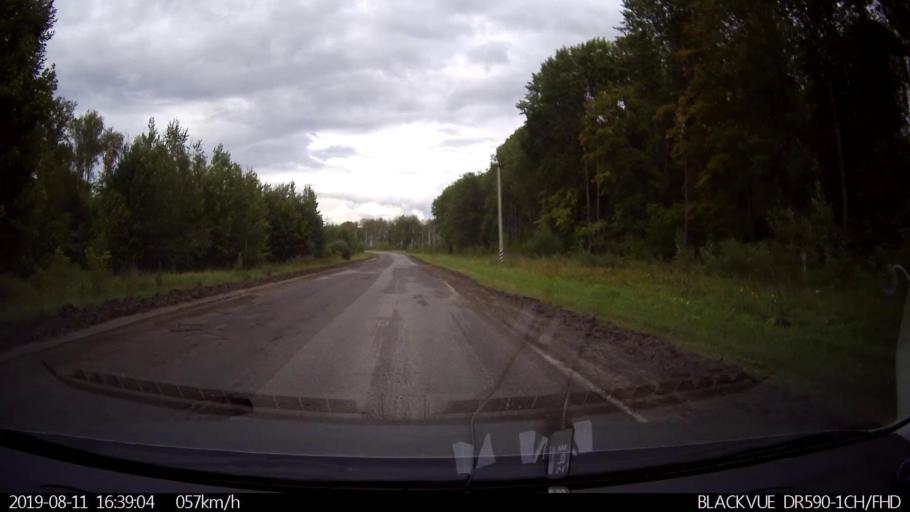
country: RU
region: Ulyanovsk
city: Mayna
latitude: 54.1379
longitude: 47.6329
